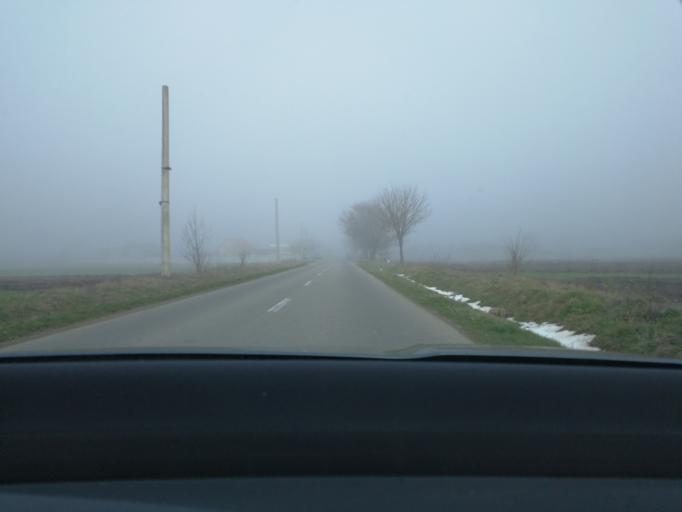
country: RO
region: Prahova
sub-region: Comuna Magureni
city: Lunca Prahovei
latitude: 45.0300
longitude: 25.7691
